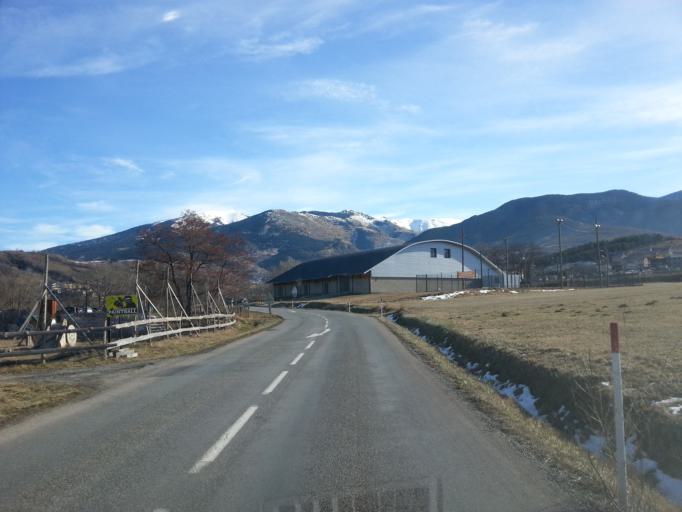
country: ES
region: Catalonia
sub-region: Provincia de Girona
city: Llivia
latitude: 42.4577
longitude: 2.0298
